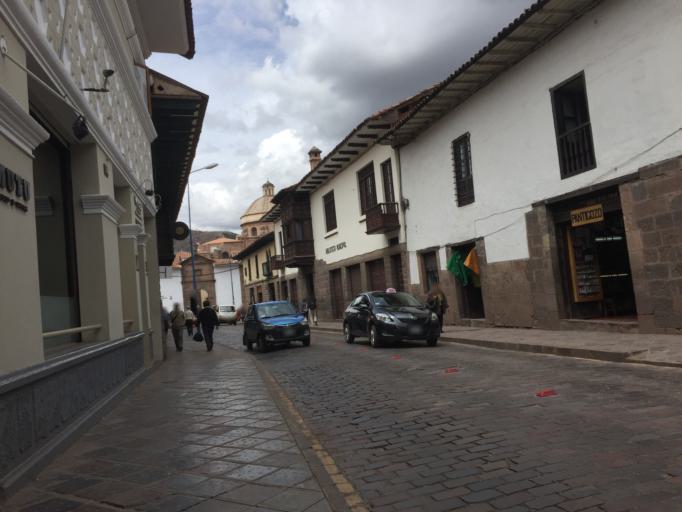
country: PE
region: Cusco
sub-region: Provincia de Cusco
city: Cusco
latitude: -13.5170
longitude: -71.9767
